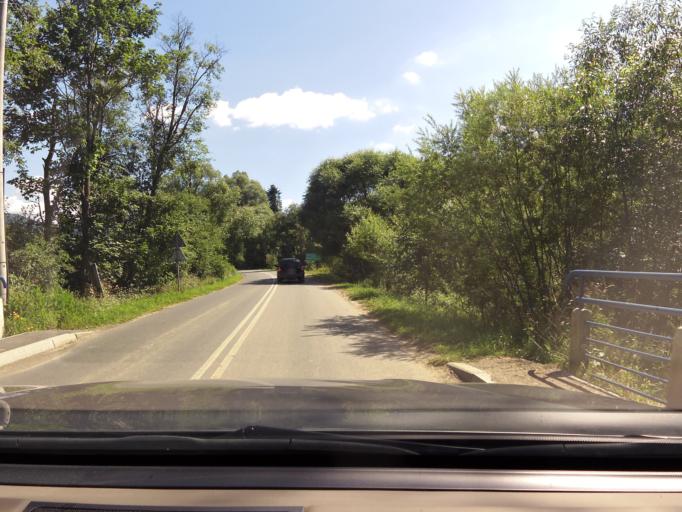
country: PL
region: Silesian Voivodeship
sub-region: Powiat zywiecki
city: Rycerka Dolna
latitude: 49.4953
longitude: 19.0822
